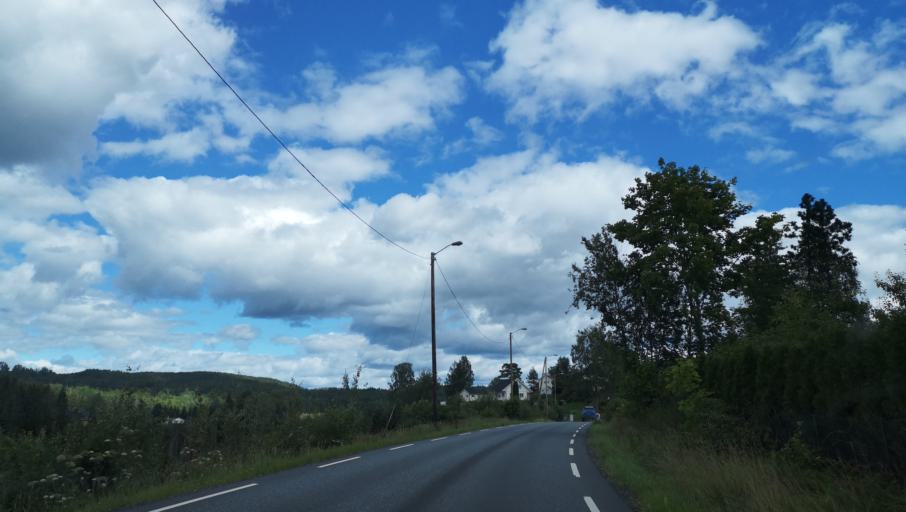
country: NO
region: Ostfold
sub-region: Hobol
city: Tomter
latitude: 59.6672
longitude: 11.0025
